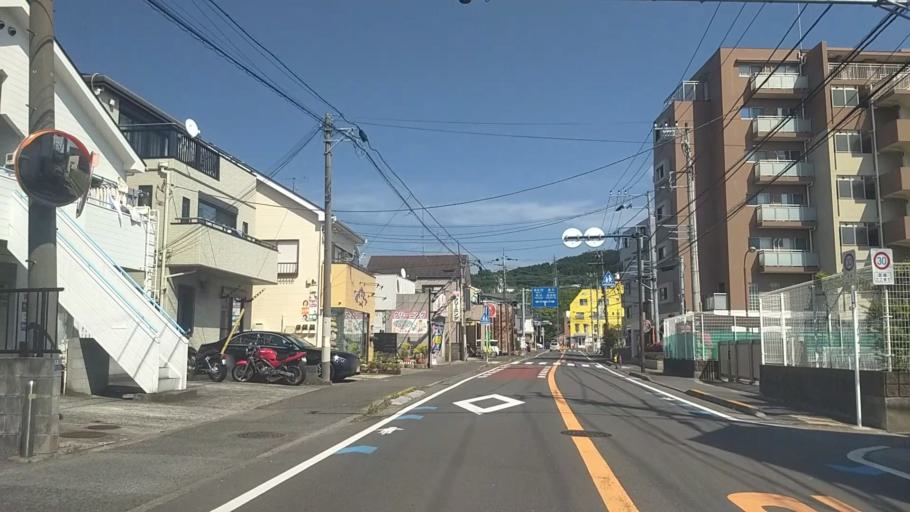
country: JP
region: Kanagawa
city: Kamakura
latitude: 35.3471
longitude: 139.5400
